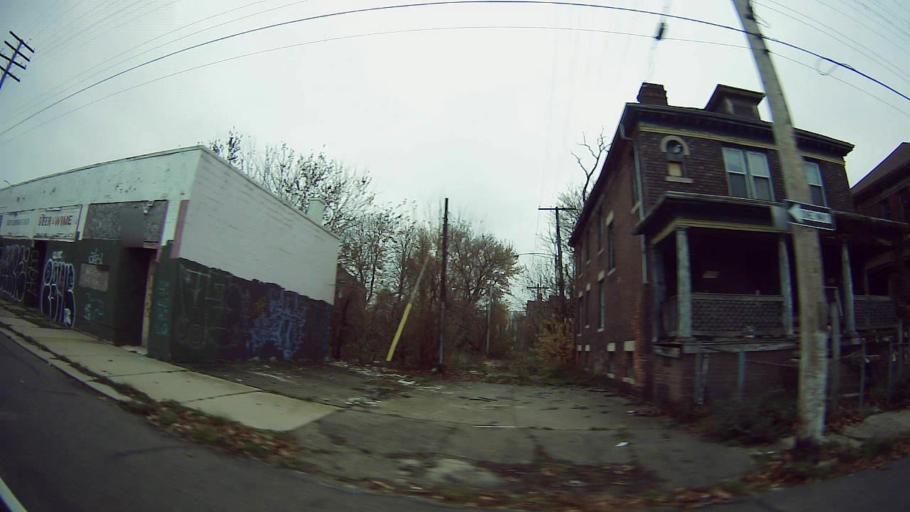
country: US
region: Michigan
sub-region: Wayne County
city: Hamtramck
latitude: 42.3784
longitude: -83.0761
